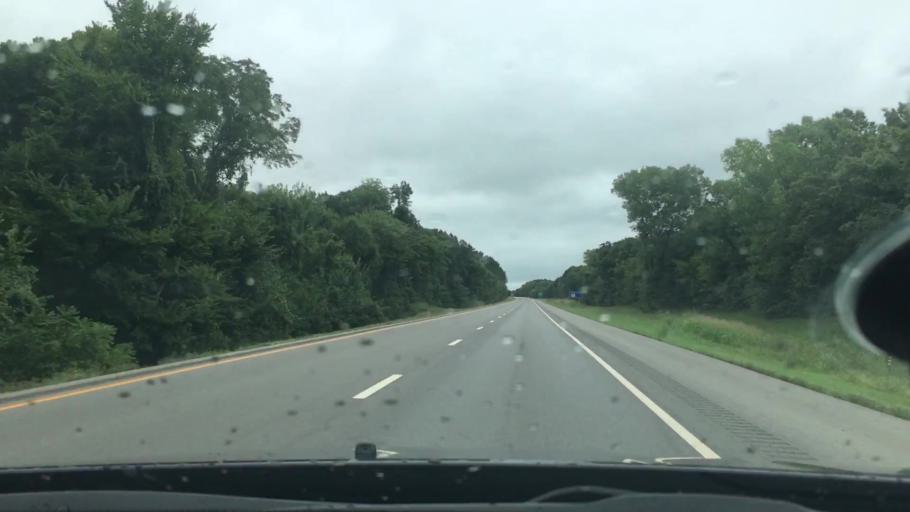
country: US
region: Oklahoma
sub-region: Okmulgee County
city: Morris
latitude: 35.4497
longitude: -95.7460
